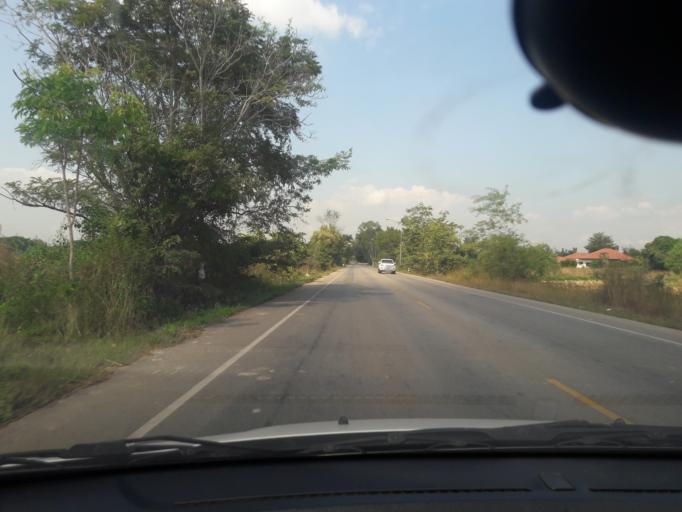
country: TH
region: Lampang
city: Mae Tha
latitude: 18.2081
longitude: 99.4973
